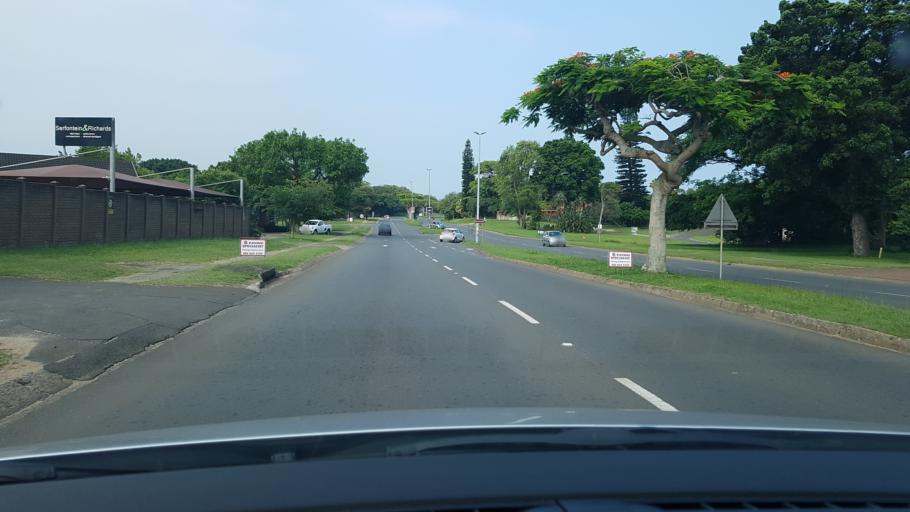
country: ZA
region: KwaZulu-Natal
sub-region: uThungulu District Municipality
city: Richards Bay
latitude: -28.7861
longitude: 32.0931
